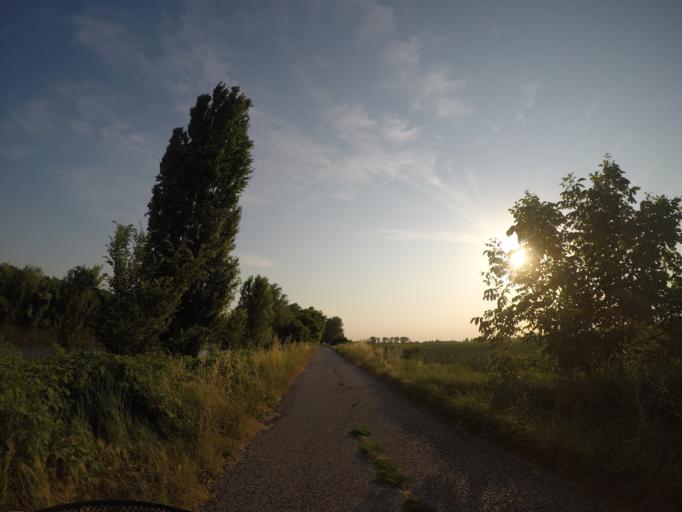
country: IT
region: Veneto
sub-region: Provincia di Rovigo
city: Fratta Polesine
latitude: 45.0090
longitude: 11.6572
